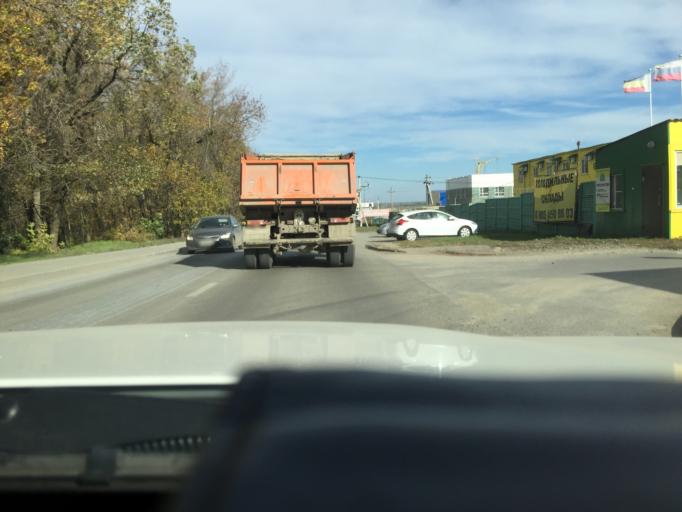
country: RU
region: Rostov
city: Imeni Chkalova
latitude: 47.2941
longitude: 39.8036
